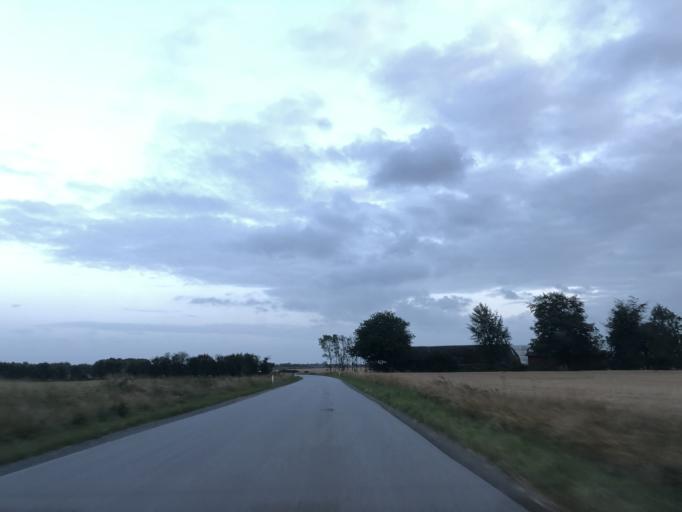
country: DK
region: South Denmark
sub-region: Haderslev Kommune
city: Starup
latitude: 55.2408
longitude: 9.6386
